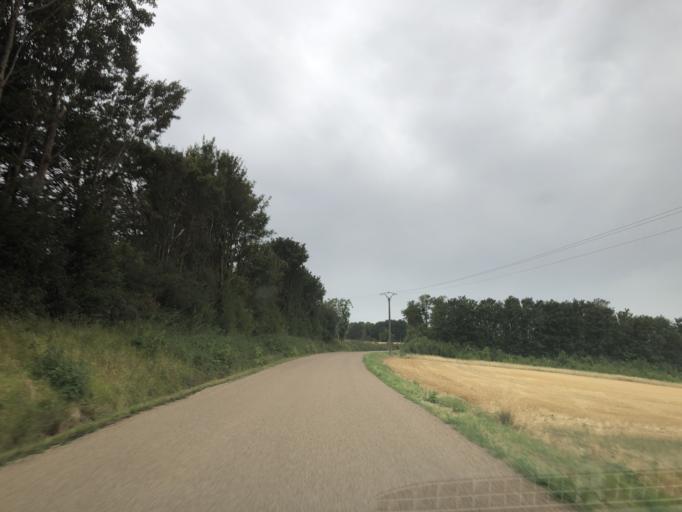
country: FR
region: Bourgogne
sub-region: Departement de l'Yonne
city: Charny
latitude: 47.9487
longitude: 3.1341
